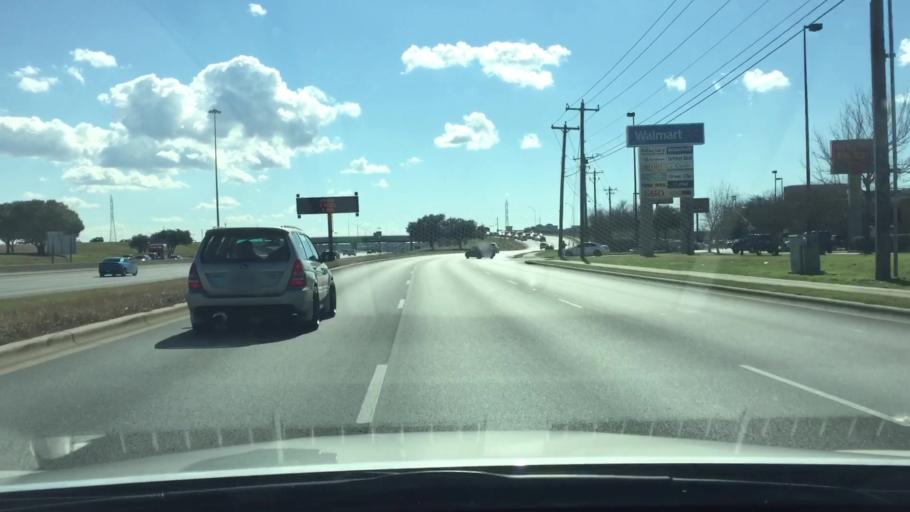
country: US
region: Texas
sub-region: Travis County
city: Wells Branch
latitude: 30.4119
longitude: -97.6747
